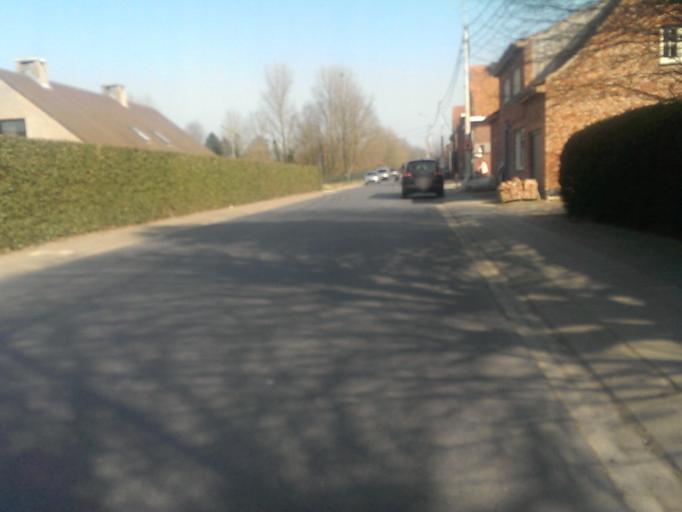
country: BE
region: Flanders
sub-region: Provincie West-Vlaanderen
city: Roeselare
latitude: 50.9285
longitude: 3.1265
